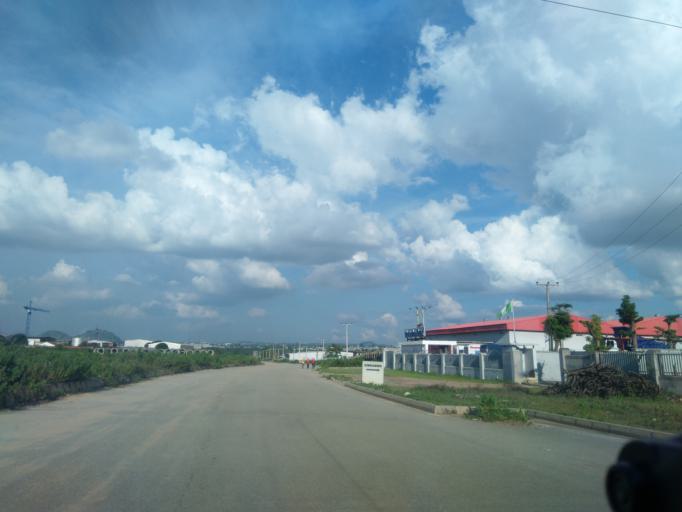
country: NG
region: Abuja Federal Capital Territory
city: Abuja
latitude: 9.0296
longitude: 7.4032
